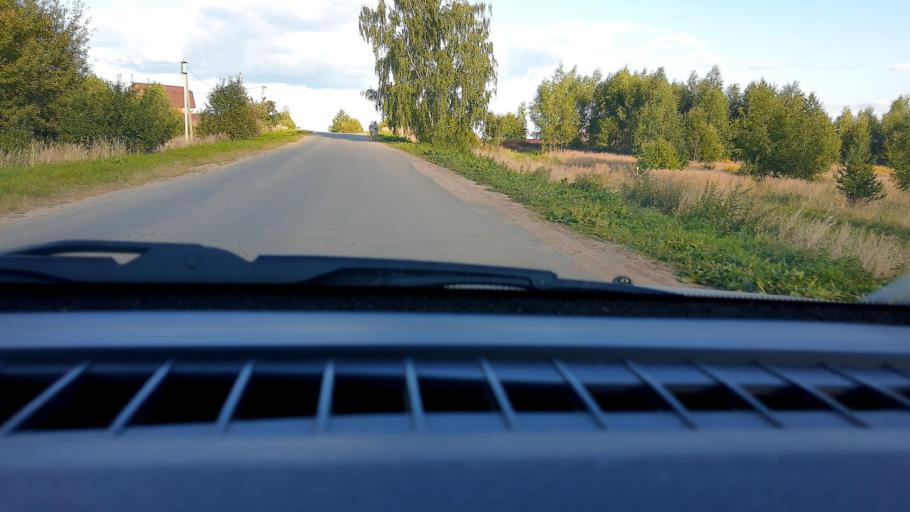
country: RU
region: Nizjnij Novgorod
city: Surovatikha
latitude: 55.9394
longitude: 43.8814
